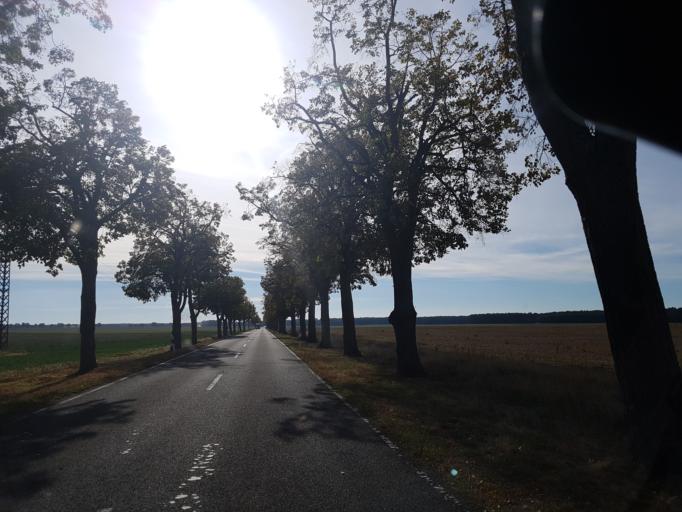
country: DE
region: Brandenburg
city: Ihlow
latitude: 51.9002
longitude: 13.2282
